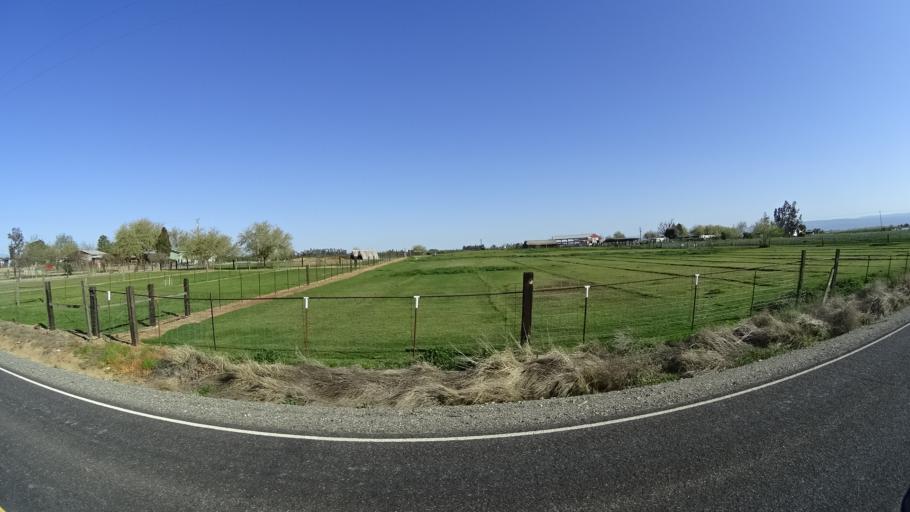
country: US
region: California
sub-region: Glenn County
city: Hamilton City
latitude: 39.7665
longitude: -122.0689
